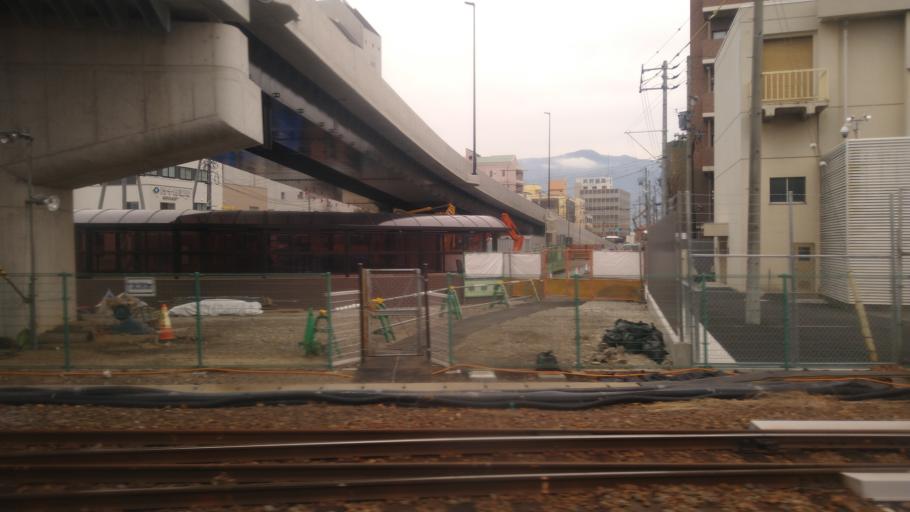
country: JP
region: Nagano
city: Matsumoto
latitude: 36.2269
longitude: 137.9667
